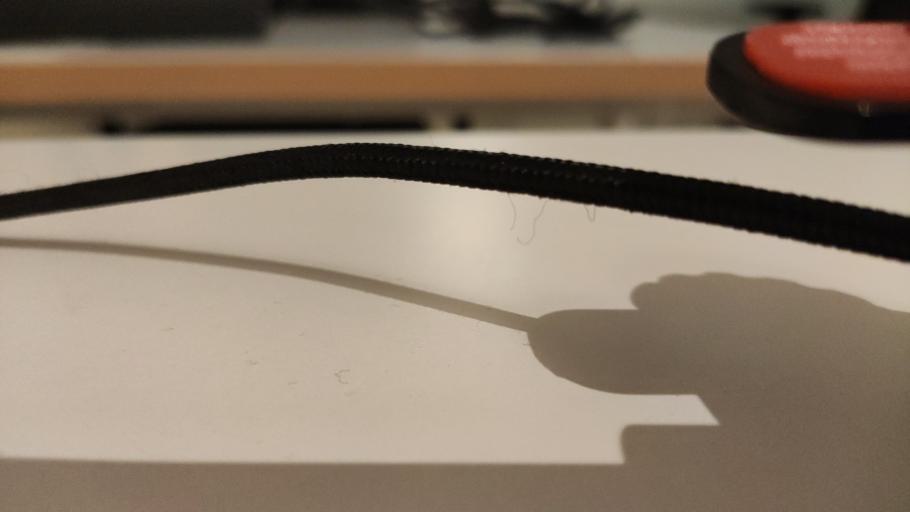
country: RU
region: Moskovskaya
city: Zhilevo
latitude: 55.0996
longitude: 38.0577
